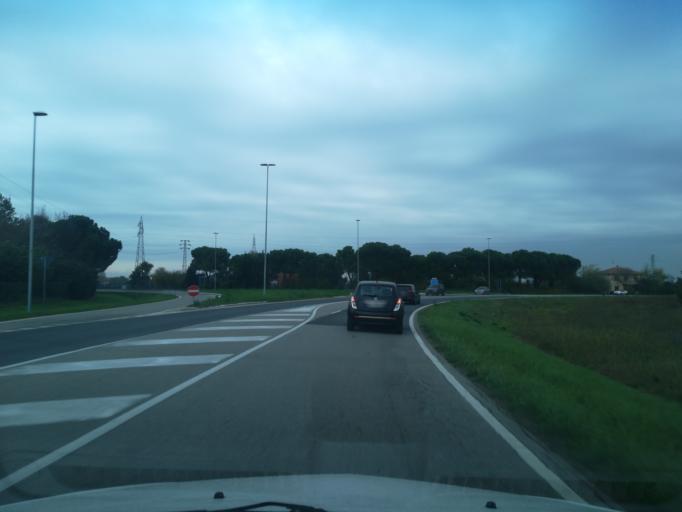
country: IT
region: Emilia-Romagna
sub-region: Provincia di Bologna
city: Imola
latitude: 44.3698
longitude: 11.7049
